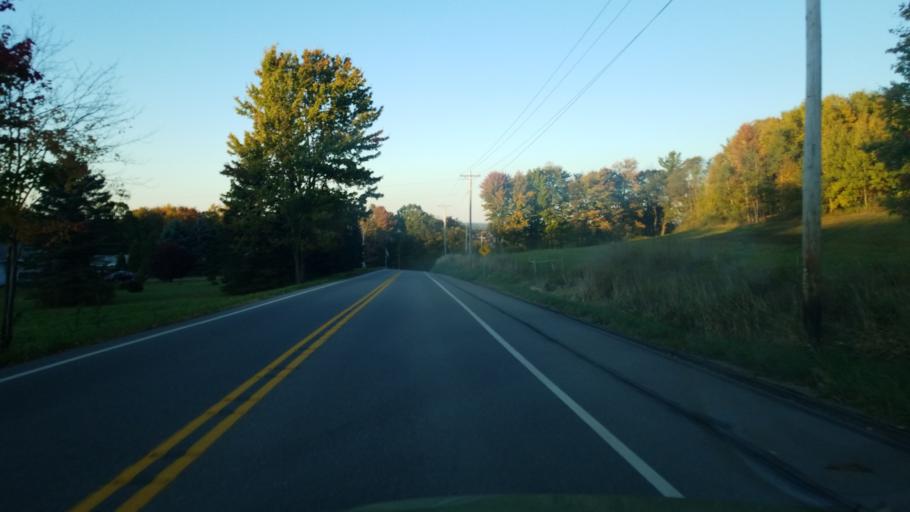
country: US
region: Pennsylvania
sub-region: Jefferson County
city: Reynoldsville
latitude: 41.0596
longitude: -78.9302
